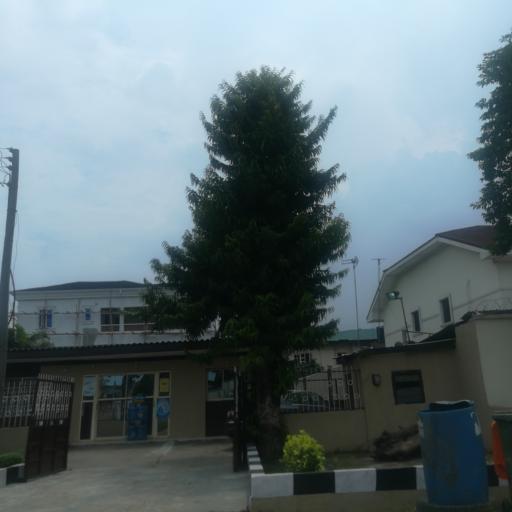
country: NG
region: Lagos
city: Ojota
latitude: 6.5773
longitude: 3.3869
